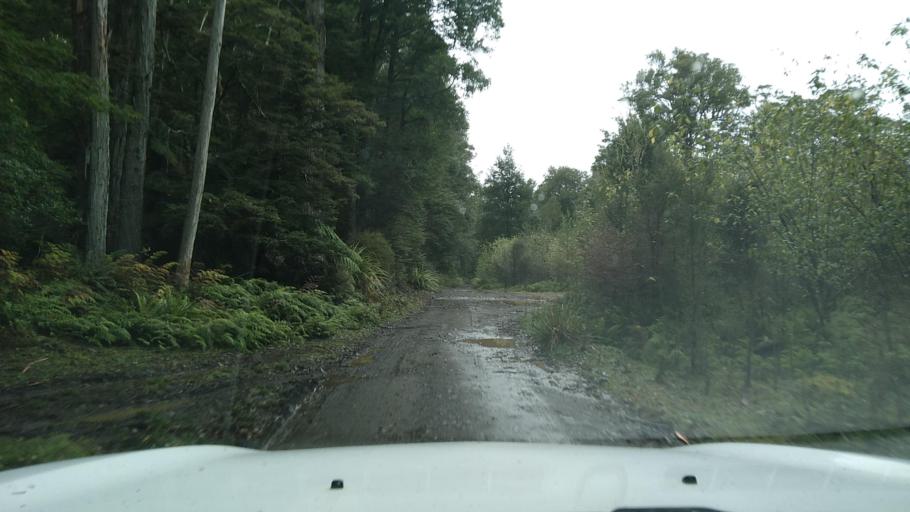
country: NZ
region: Manawatu-Wanganui
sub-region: Ruapehu District
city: Waiouru
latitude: -39.4201
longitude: 175.5063
